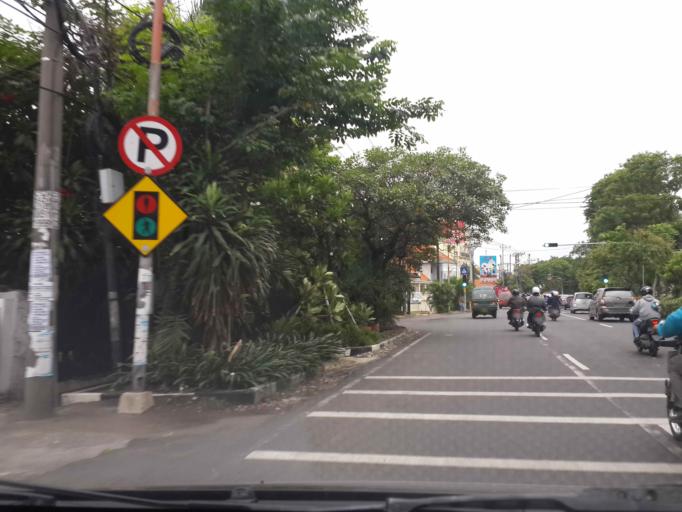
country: ID
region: East Java
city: Gubengairlangga
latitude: -7.2804
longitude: 112.7313
